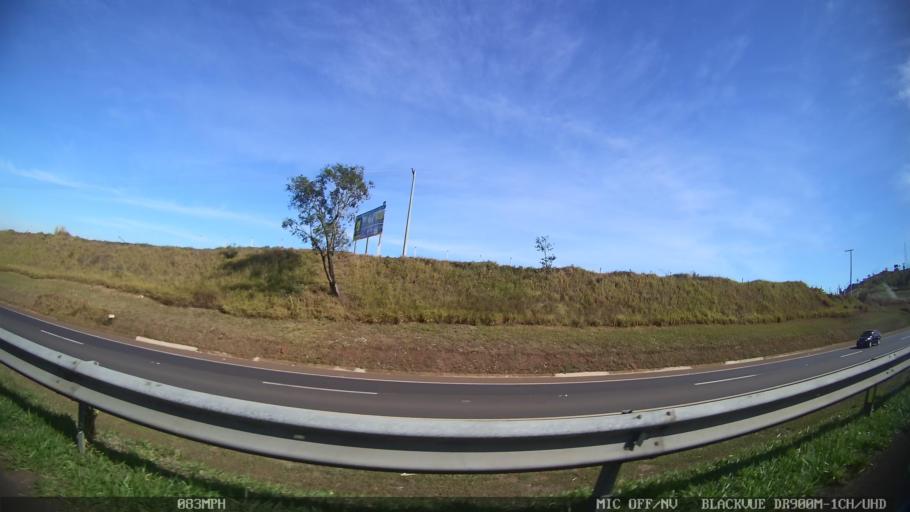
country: BR
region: Sao Paulo
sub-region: Leme
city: Leme
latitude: -22.1643
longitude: -47.3996
